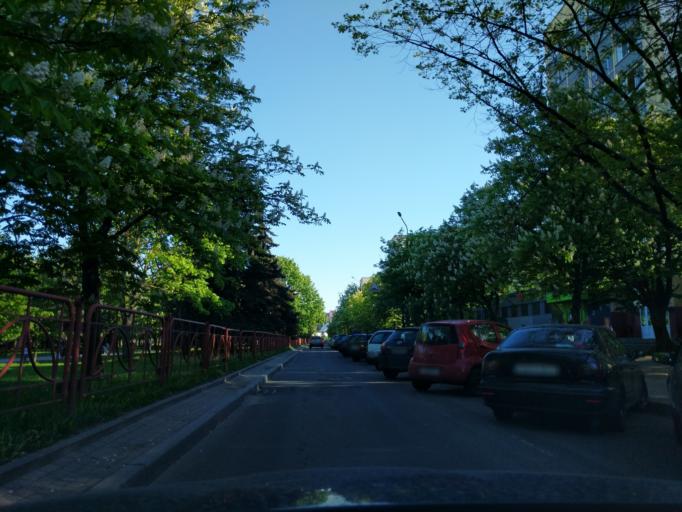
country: BY
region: Minsk
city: Novoye Medvezhino
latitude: 53.9118
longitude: 27.4873
